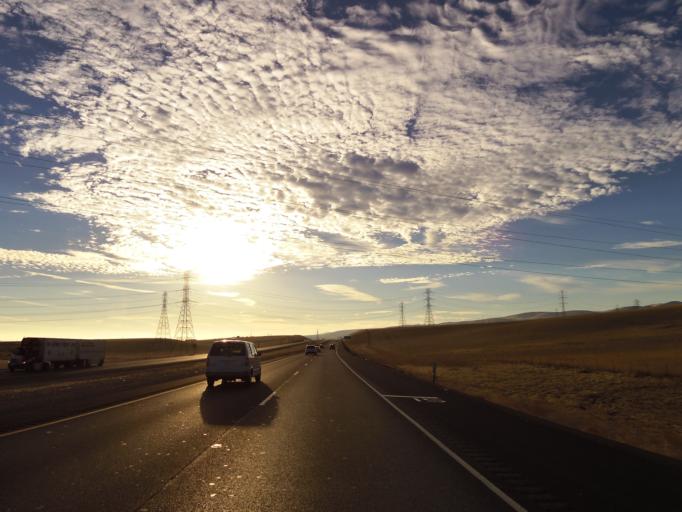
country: US
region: California
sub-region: San Joaquin County
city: Mountain House
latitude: 37.7356
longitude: -121.5535
